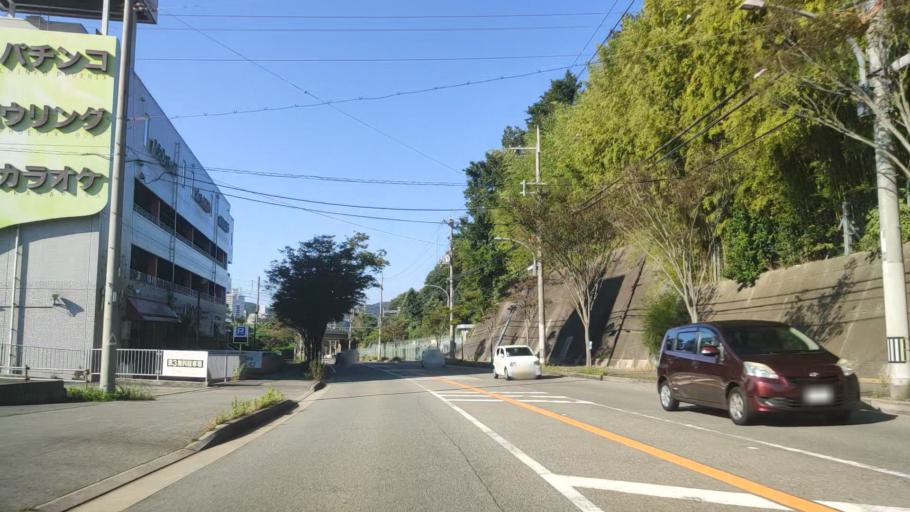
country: JP
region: Hyogo
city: Kobe
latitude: 34.7731
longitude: 135.1928
